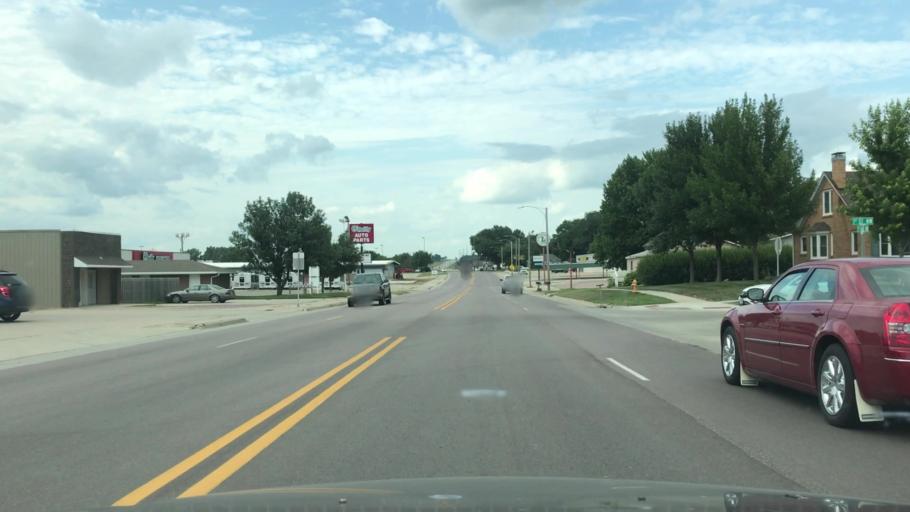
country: US
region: Iowa
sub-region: Plymouth County
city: Le Mars
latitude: 42.7941
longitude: -96.1738
